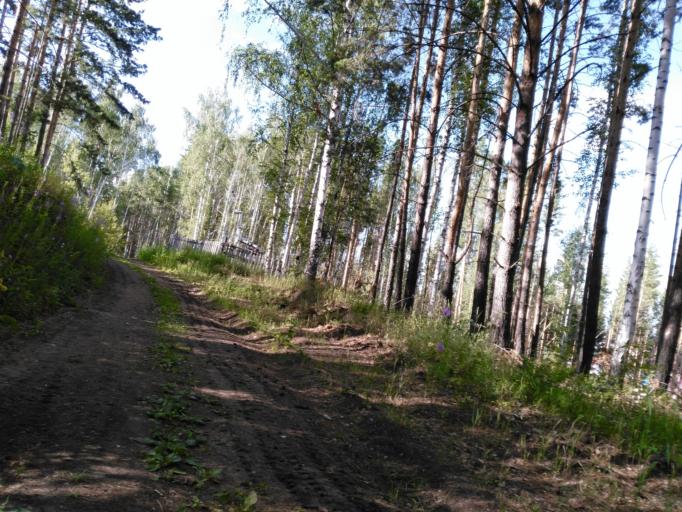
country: RU
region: Bashkortostan
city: Uchaly
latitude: 54.3277
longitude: 59.3604
